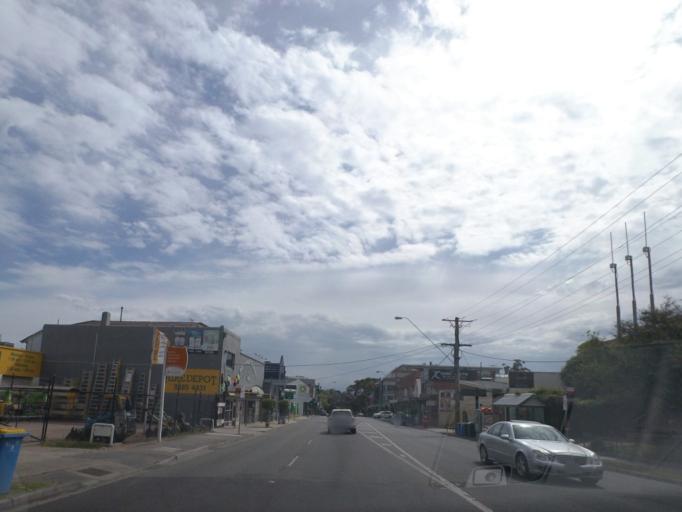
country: AU
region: Victoria
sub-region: Boroondara
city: Ashburton
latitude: -37.8619
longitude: 145.0671
